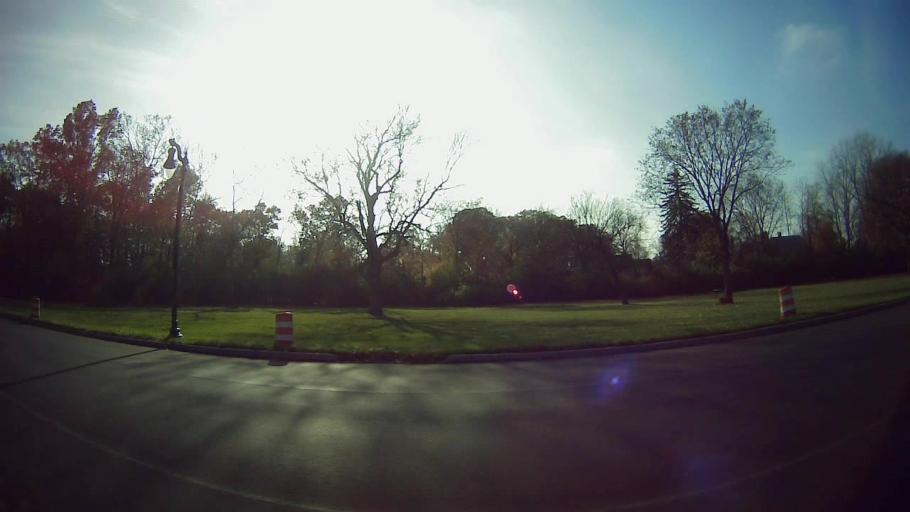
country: US
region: Michigan
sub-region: Wayne County
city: Highland Park
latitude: 42.4255
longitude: -83.1224
